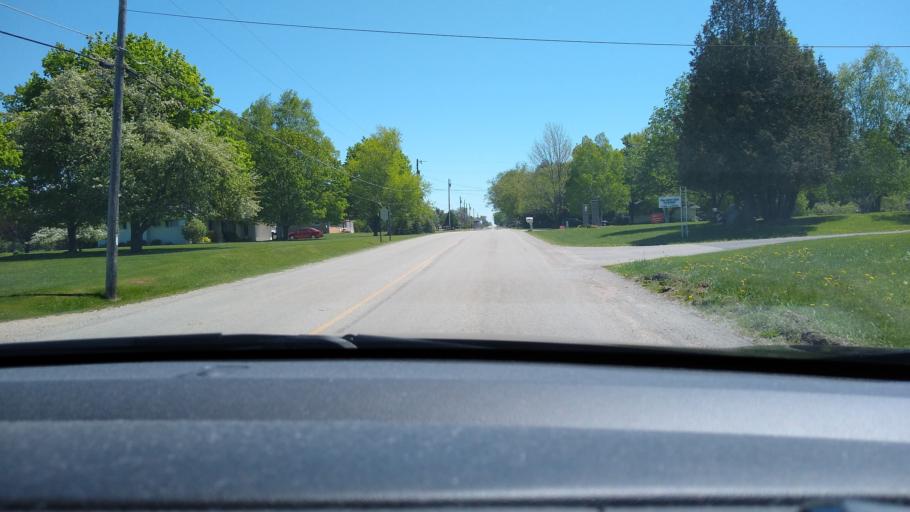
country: US
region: Michigan
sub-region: Delta County
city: Escanaba
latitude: 45.8260
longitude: -87.1820
